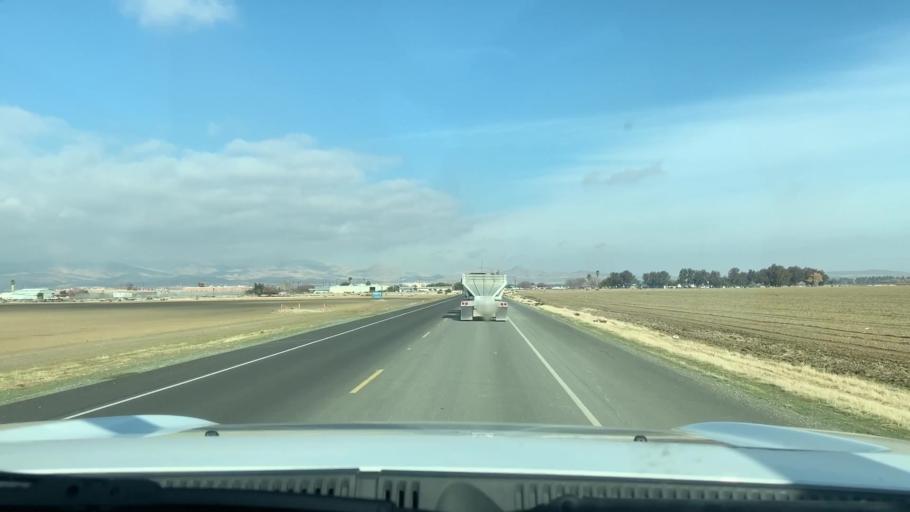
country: US
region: California
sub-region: Fresno County
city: Coalinga
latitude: 36.1733
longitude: -120.3546
